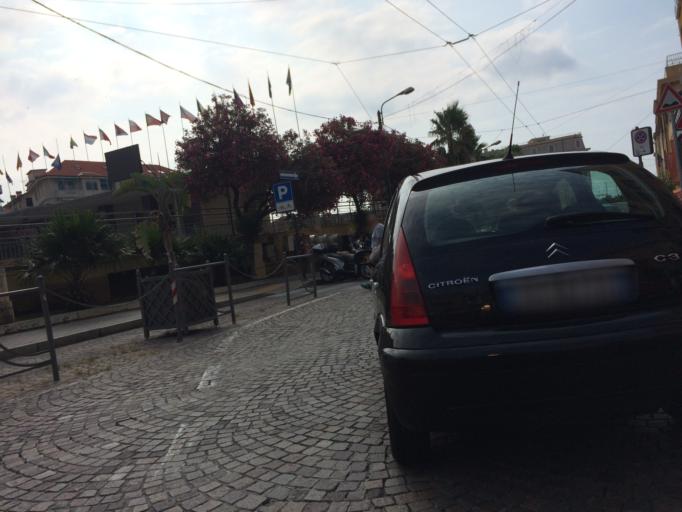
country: IT
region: Liguria
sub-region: Provincia di Imperia
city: San Remo
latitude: 43.8183
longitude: 7.7778
